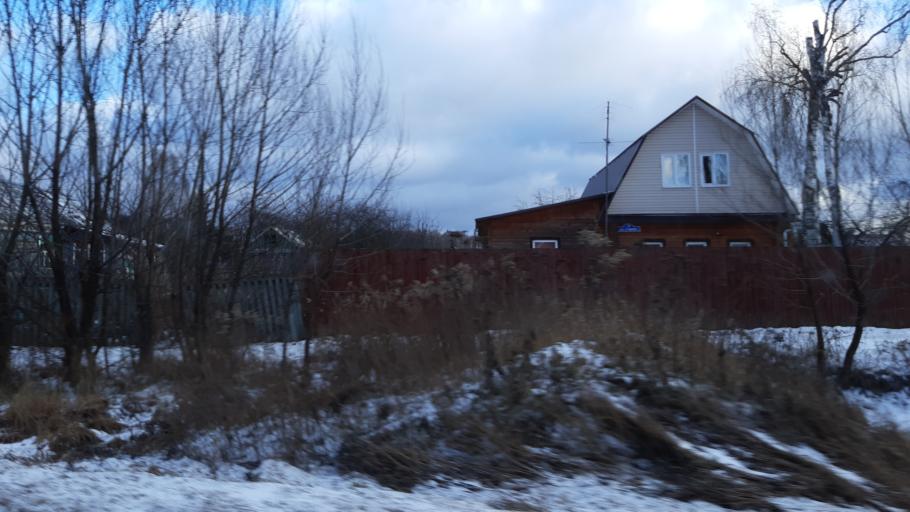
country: RU
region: Moskovskaya
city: Noginsk-9
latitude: 55.9950
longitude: 38.5435
